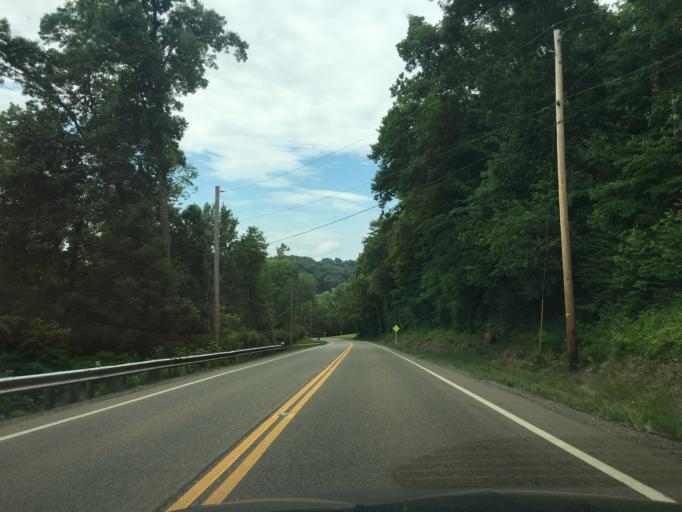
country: US
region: Ohio
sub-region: Tuscarawas County
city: New Philadelphia
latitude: 40.5259
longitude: -81.4256
